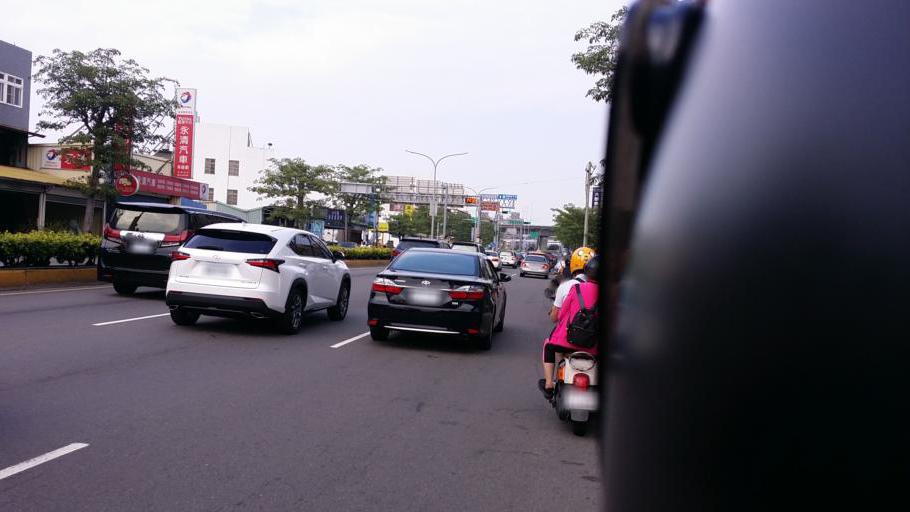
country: TW
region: Taiwan
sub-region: Hsinchu
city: Zhubei
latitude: 24.8166
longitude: 120.9937
